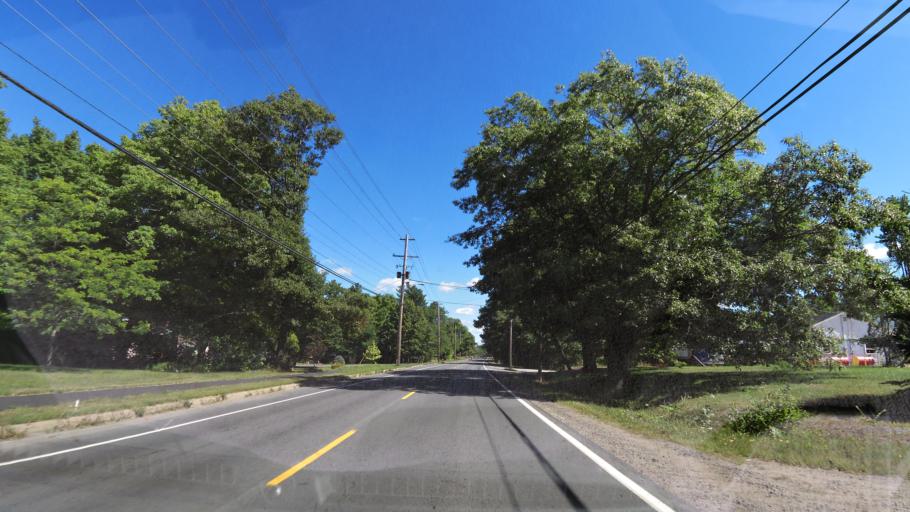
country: CA
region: Nova Scotia
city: Berwick
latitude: 45.0588
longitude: -64.6188
